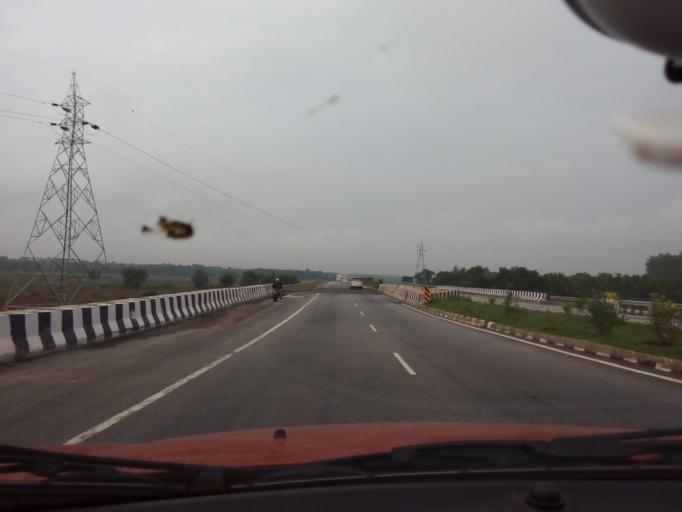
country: IN
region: Karnataka
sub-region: Tumkur
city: Kunigal
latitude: 13.0151
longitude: 77.0415
